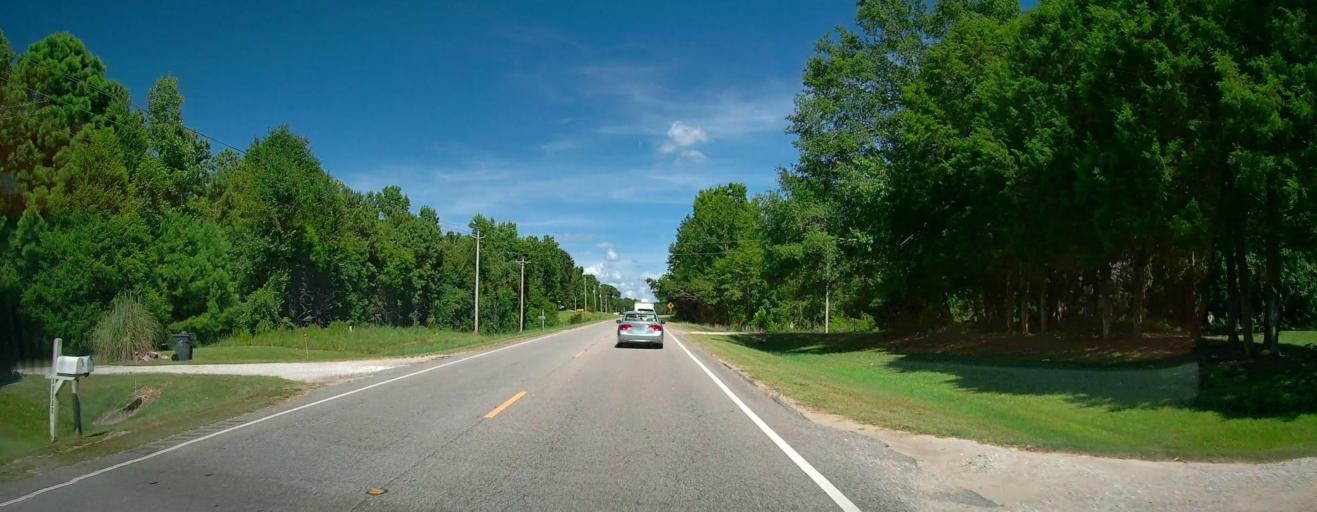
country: US
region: Alabama
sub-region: Elmore County
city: Tallassee
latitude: 32.3986
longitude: -85.9237
